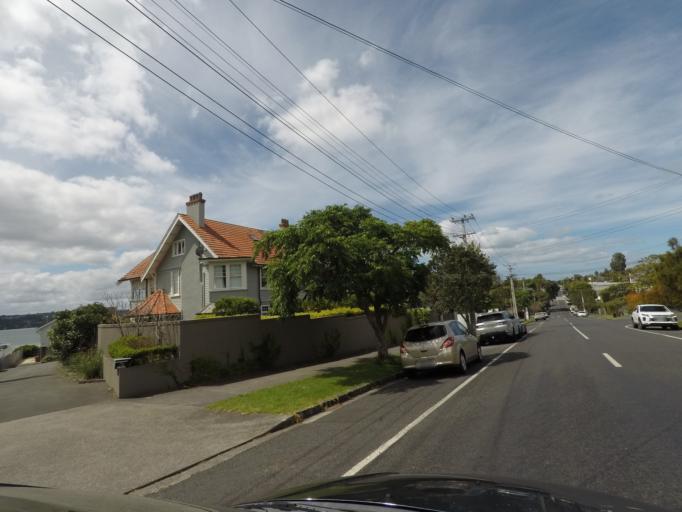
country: NZ
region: Auckland
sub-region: Auckland
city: Auckland
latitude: -36.8449
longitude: 174.7281
